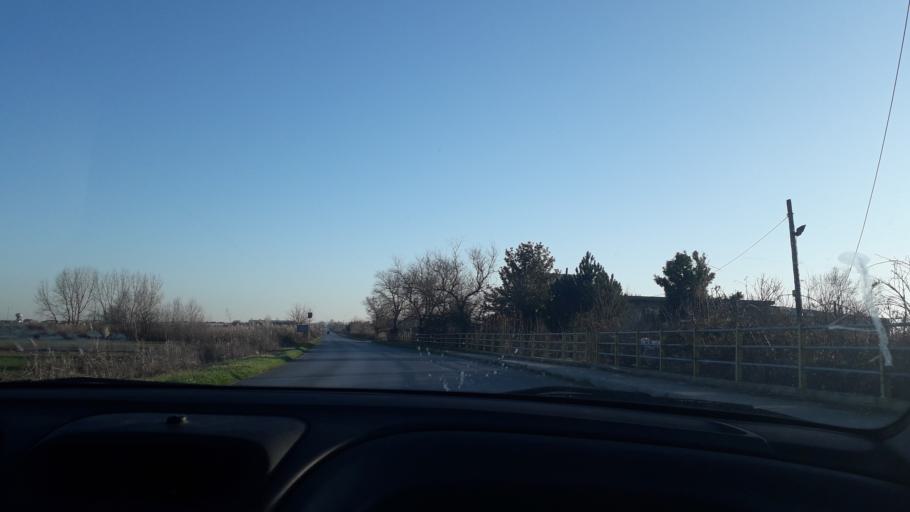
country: GR
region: Central Macedonia
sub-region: Nomos Imathias
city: Alexandreia
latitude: 40.6450
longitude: 22.4350
